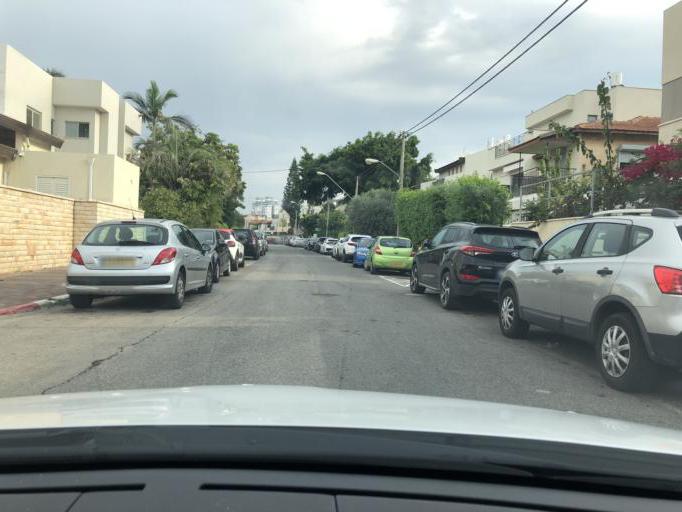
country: IL
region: Tel Aviv
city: Giv`atayim
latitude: 32.0547
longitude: 34.8236
